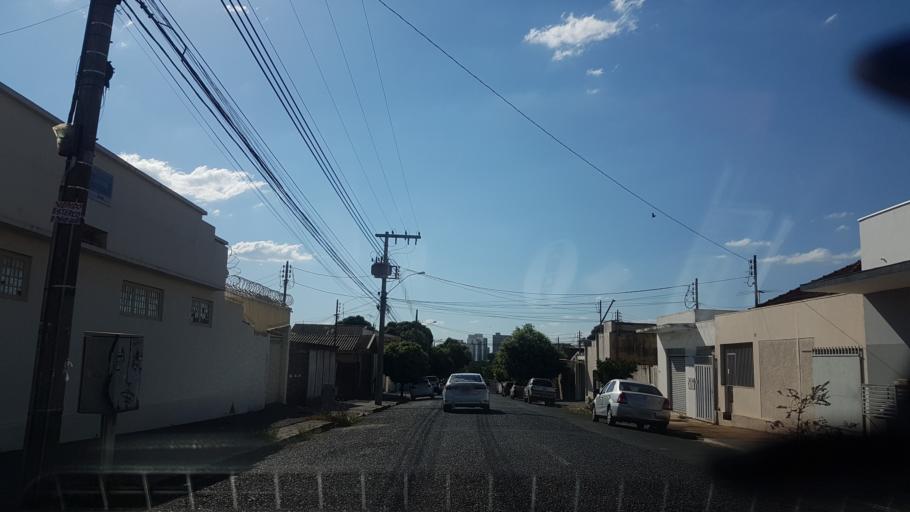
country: BR
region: Minas Gerais
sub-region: Uberlandia
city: Uberlandia
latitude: -18.9095
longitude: -48.2840
